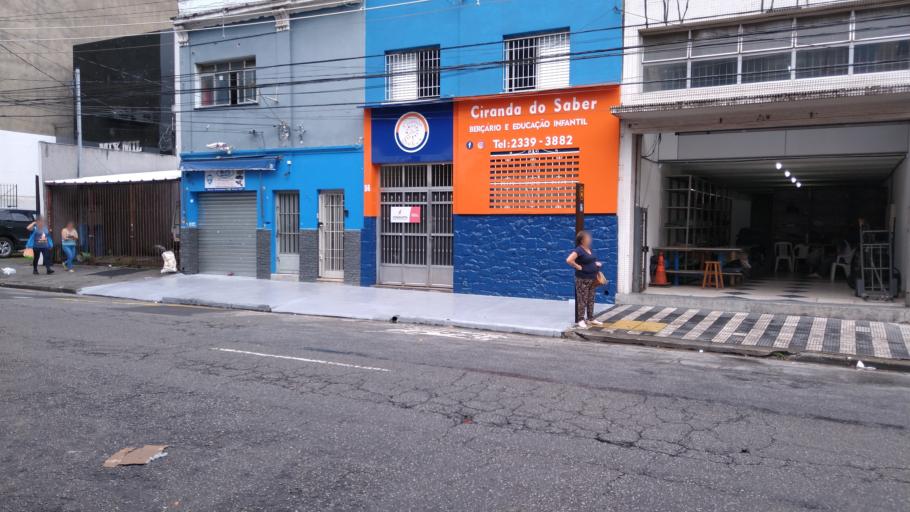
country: BR
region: Sao Paulo
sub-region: Sao Paulo
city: Sao Paulo
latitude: -23.5336
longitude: -46.6173
